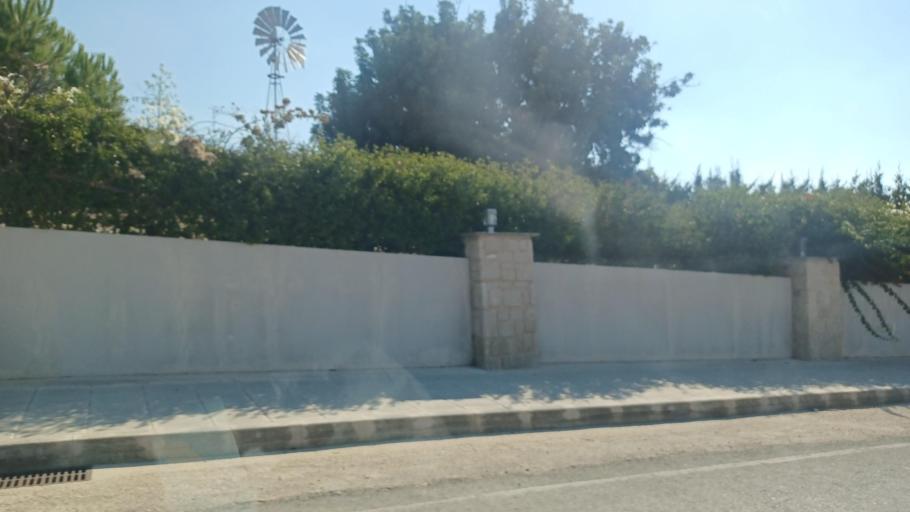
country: CY
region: Pafos
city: Tala
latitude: 34.8307
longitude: 32.4462
